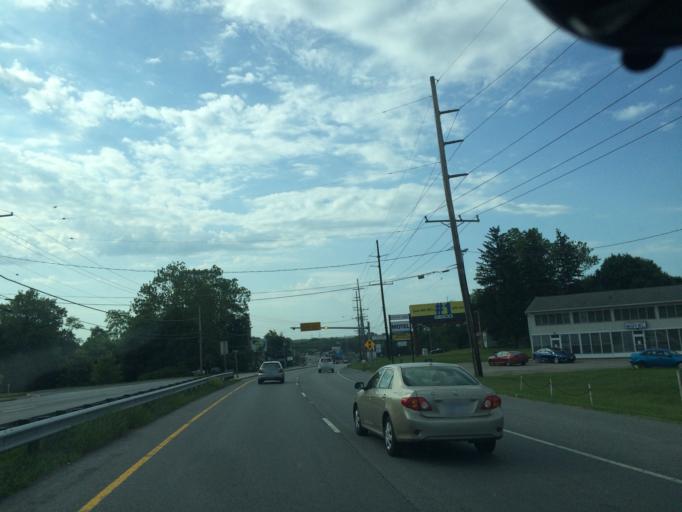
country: US
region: Maryland
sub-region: Baltimore County
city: Reisterstown
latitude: 39.4992
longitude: -76.8948
